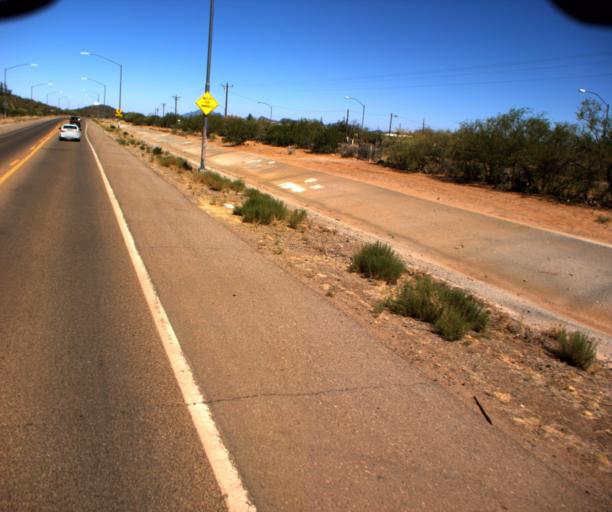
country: US
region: Arizona
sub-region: Pima County
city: Sells
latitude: 31.9170
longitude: -111.8709
